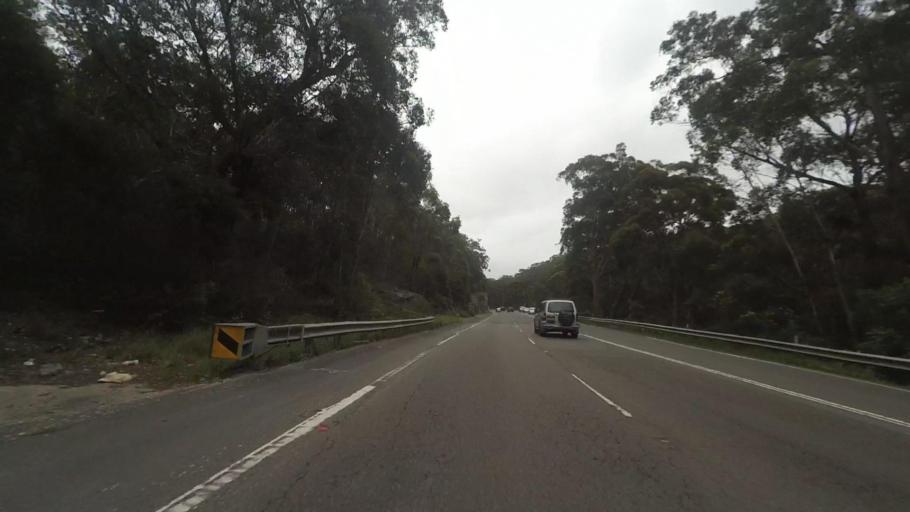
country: AU
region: New South Wales
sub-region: Sutherland Shire
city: Engadine
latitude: -34.0577
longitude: 150.9857
